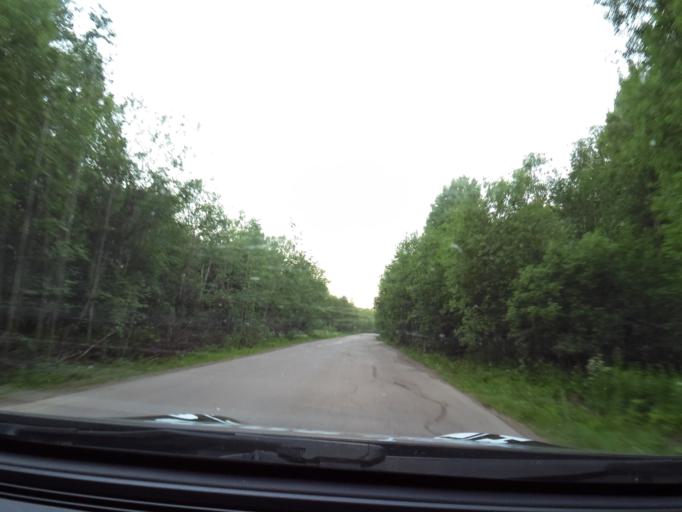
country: RU
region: Leningrad
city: Voznesen'ye
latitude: 60.9551
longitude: 35.4712
